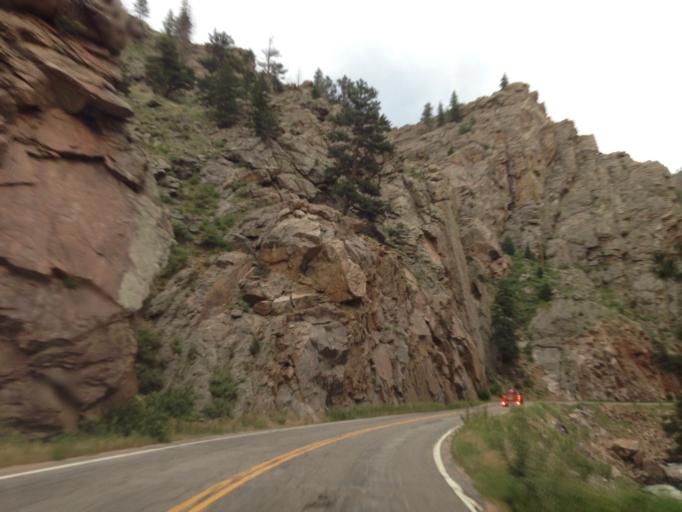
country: US
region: Colorado
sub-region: Larimer County
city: Laporte
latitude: 40.6778
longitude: -105.4309
